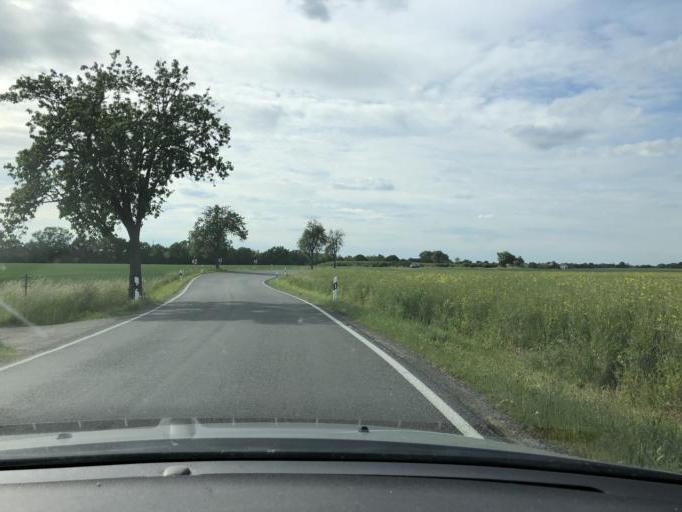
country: DE
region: Saxony
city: Nerchau
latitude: 51.2781
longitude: 12.7820
